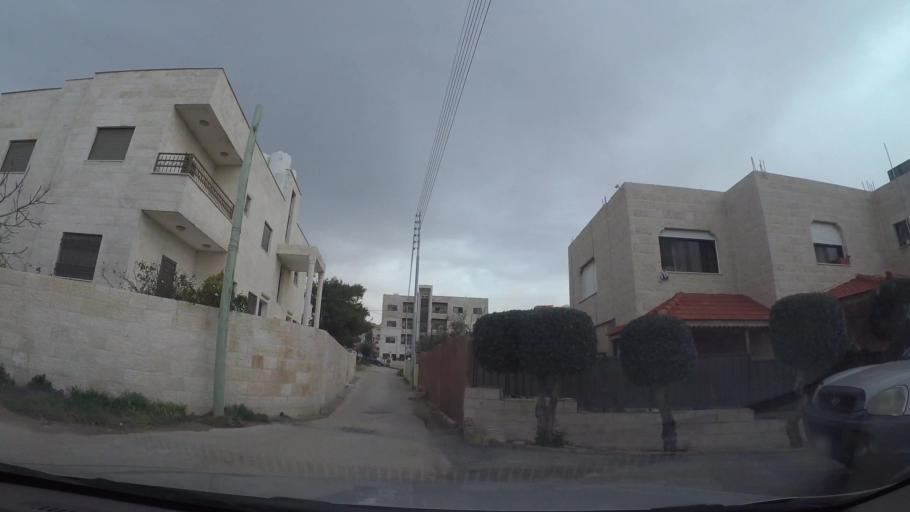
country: JO
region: Amman
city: Umm as Summaq
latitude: 31.9041
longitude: 35.8344
